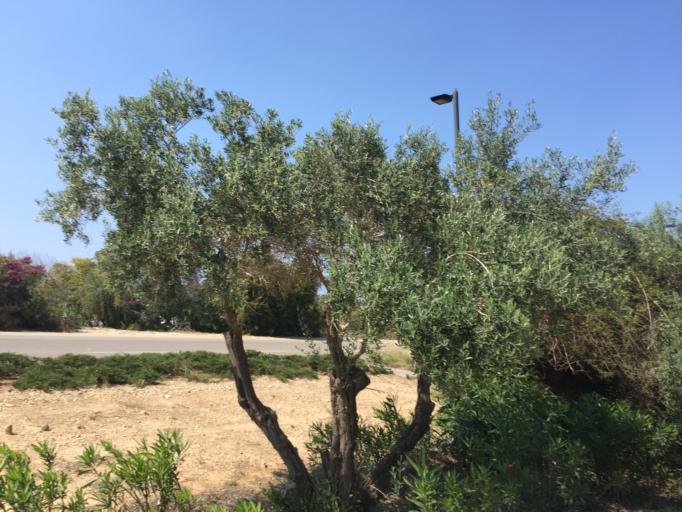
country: IL
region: Haifa
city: Qesarya
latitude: 32.4919
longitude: 34.9039
